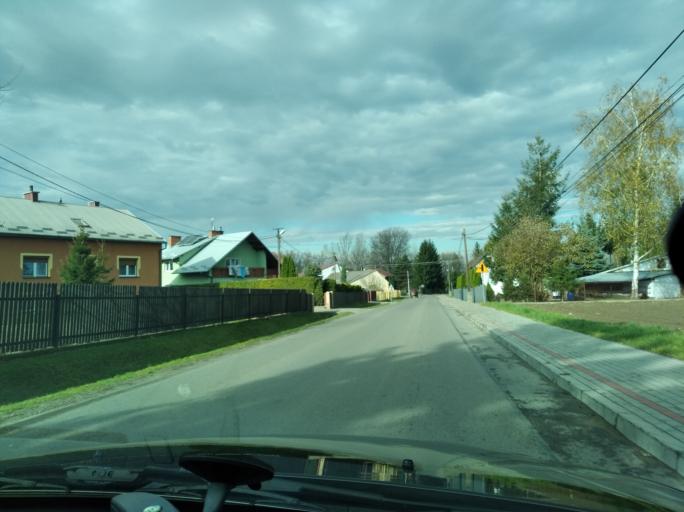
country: PL
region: Subcarpathian Voivodeship
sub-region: Powiat debicki
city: Brzeznica
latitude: 50.0820
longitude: 21.5226
